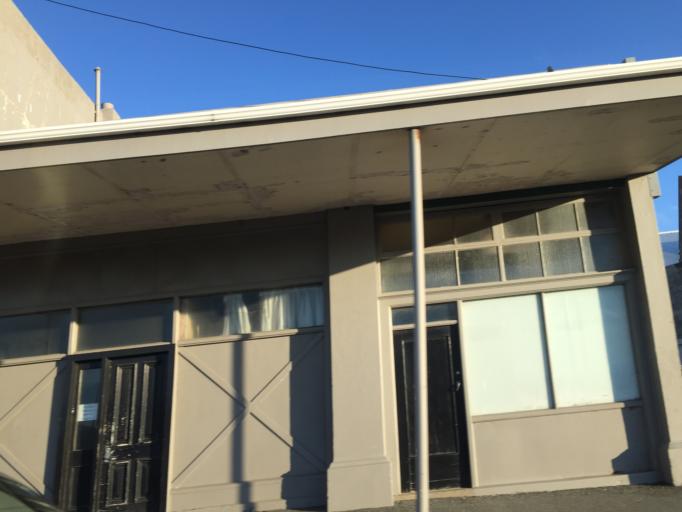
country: NZ
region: Southland
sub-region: Invercargill City
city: Bluff
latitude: -46.5988
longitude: 168.3417
